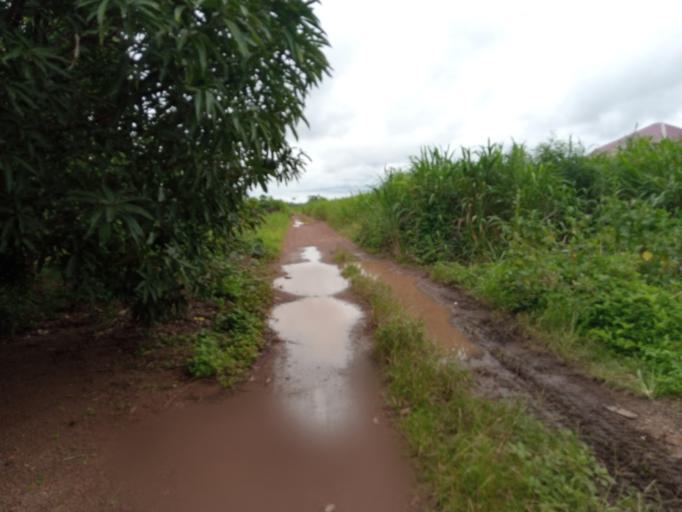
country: SL
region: Southern Province
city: Largo
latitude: 8.1969
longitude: -12.0479
